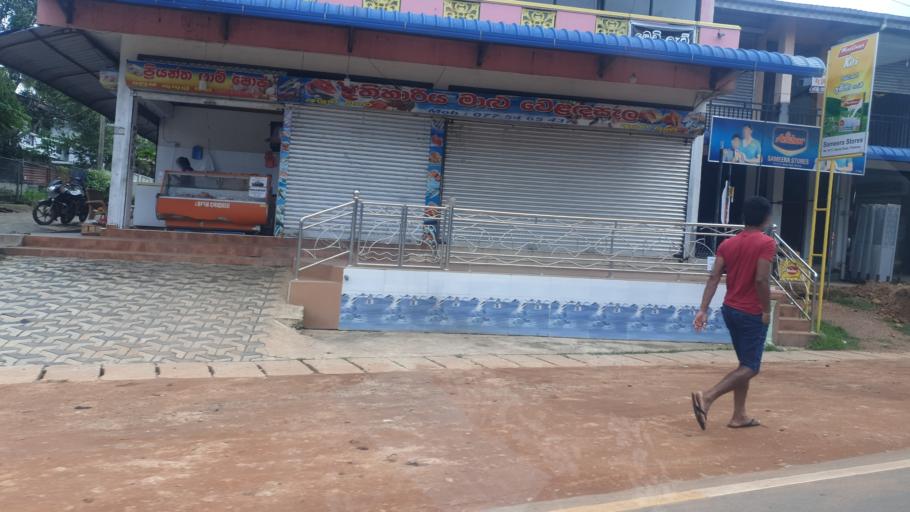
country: LK
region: Western
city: Gampaha
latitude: 7.1242
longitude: 80.0686
